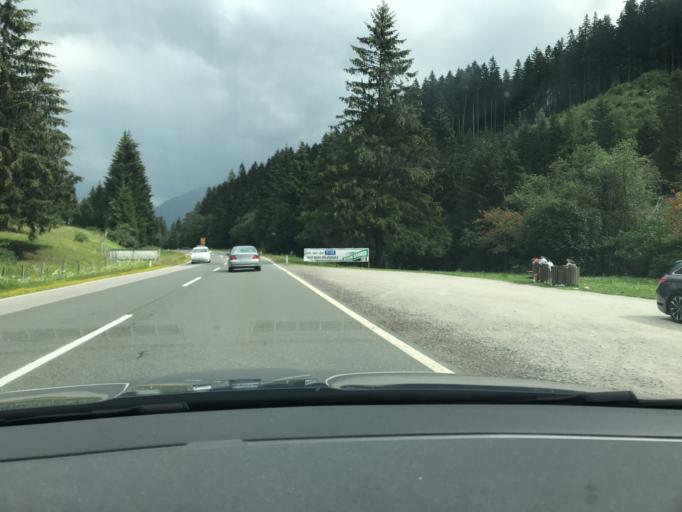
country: AT
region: Tyrol
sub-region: Politischer Bezirk Lienz
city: Matrei in Osttirol
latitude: 46.9652
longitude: 12.5515
